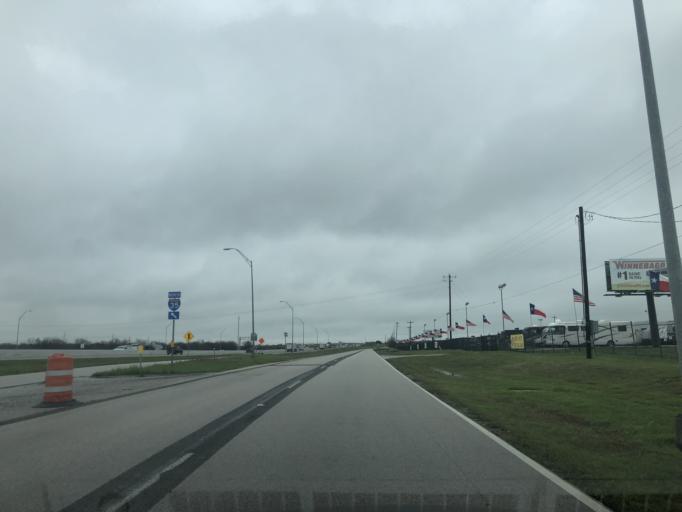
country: US
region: Texas
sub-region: Williamson County
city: Serenada
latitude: 30.7262
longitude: -97.6427
